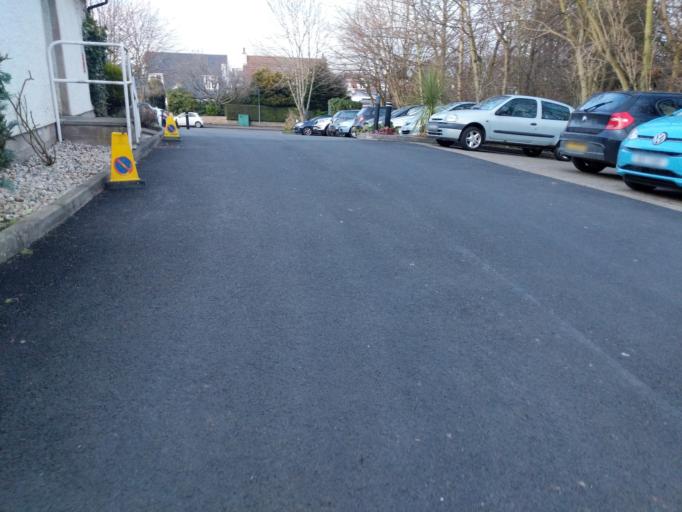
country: GB
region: Scotland
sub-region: Edinburgh
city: Colinton
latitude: 55.9553
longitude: -3.2632
